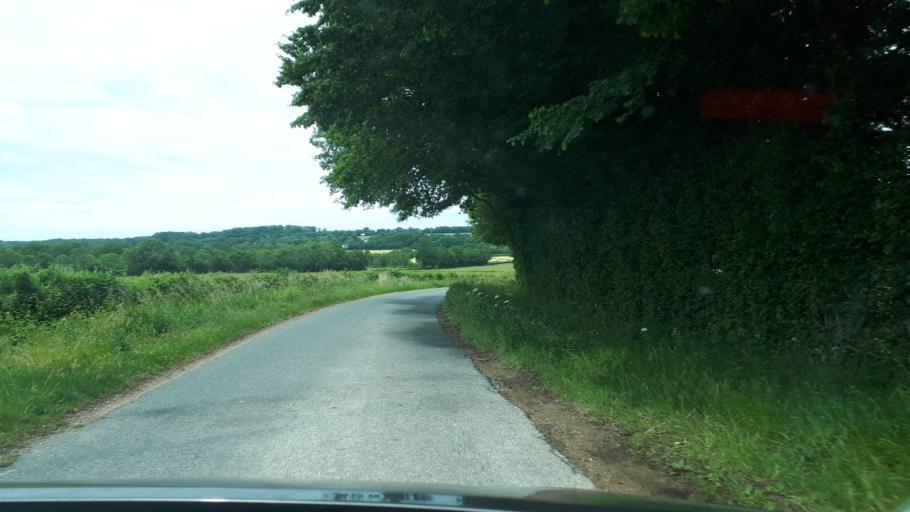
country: FR
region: Centre
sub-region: Departement du Cher
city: Henrichemont
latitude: 47.4110
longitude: 2.6288
